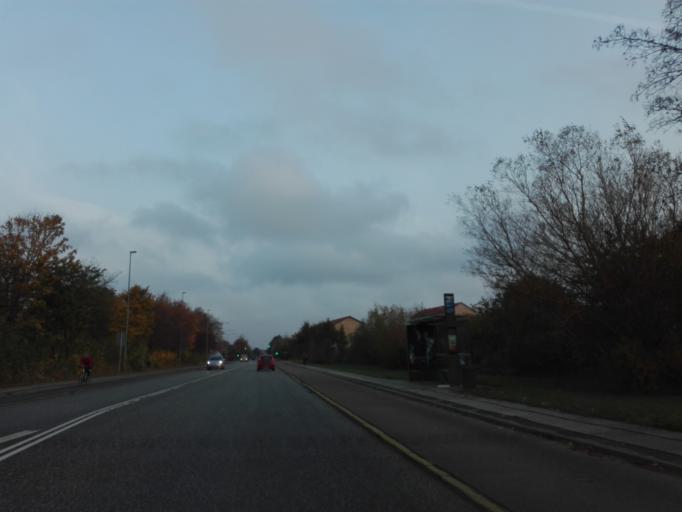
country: DK
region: Central Jutland
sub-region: Arhus Kommune
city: Beder
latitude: 56.1079
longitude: 10.2078
